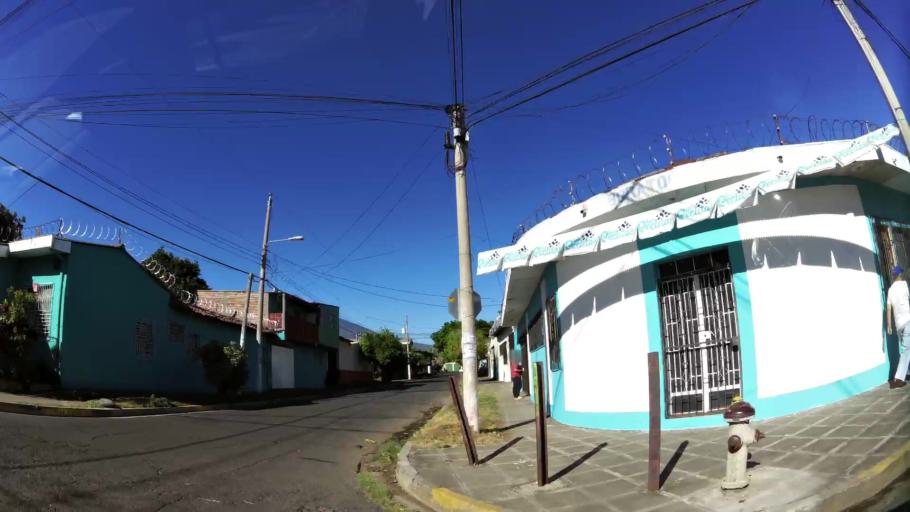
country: SV
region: San Miguel
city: San Miguel
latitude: 13.4738
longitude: -88.1772
